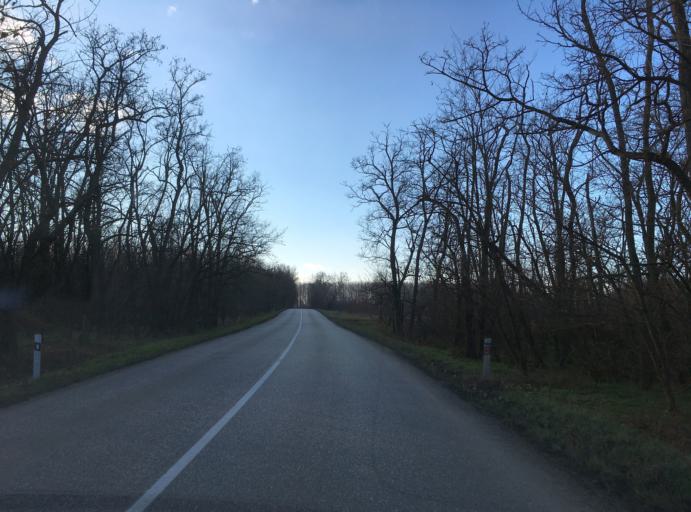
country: SK
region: Nitriansky
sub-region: Okres Komarno
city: Hurbanovo
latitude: 47.8322
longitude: 18.2384
